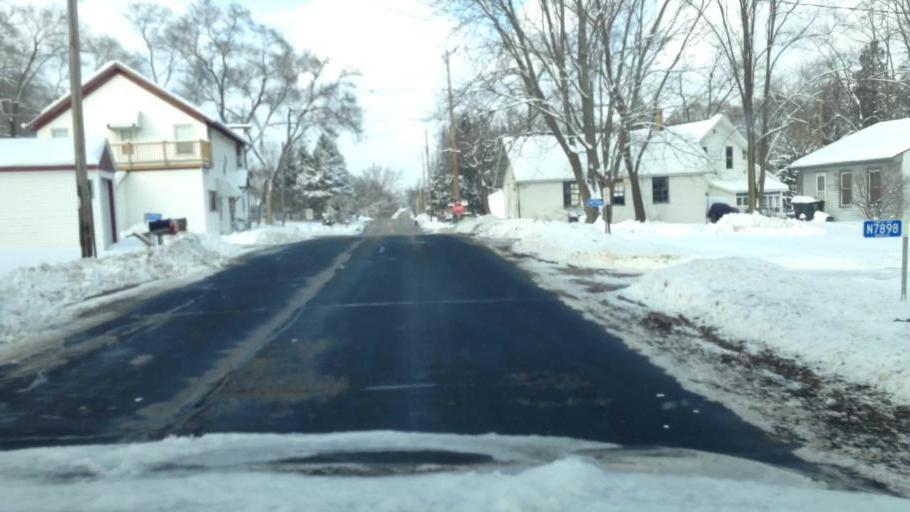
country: US
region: Wisconsin
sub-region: Walworth County
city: East Troy
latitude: 42.7780
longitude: -88.4451
